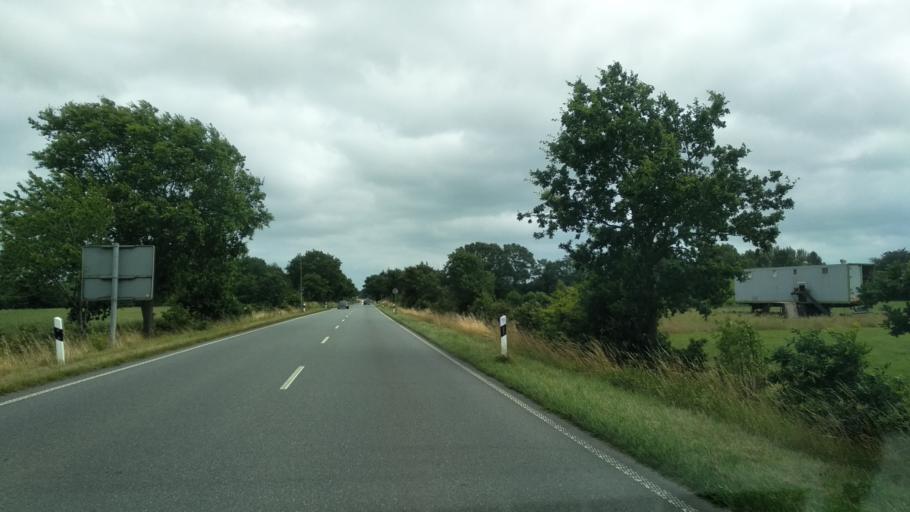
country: DE
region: Schleswig-Holstein
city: Neuberend
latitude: 54.5464
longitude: 9.5453
